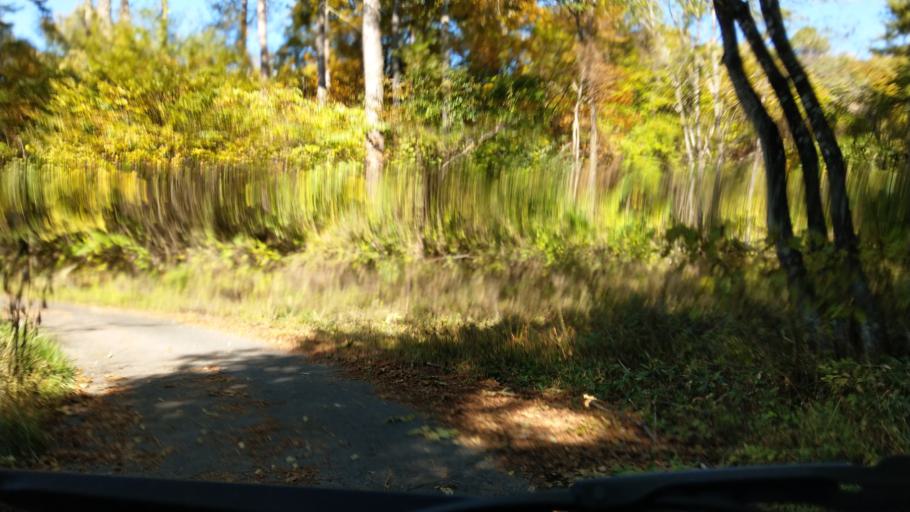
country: JP
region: Nagano
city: Komoro
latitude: 36.3690
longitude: 138.4446
